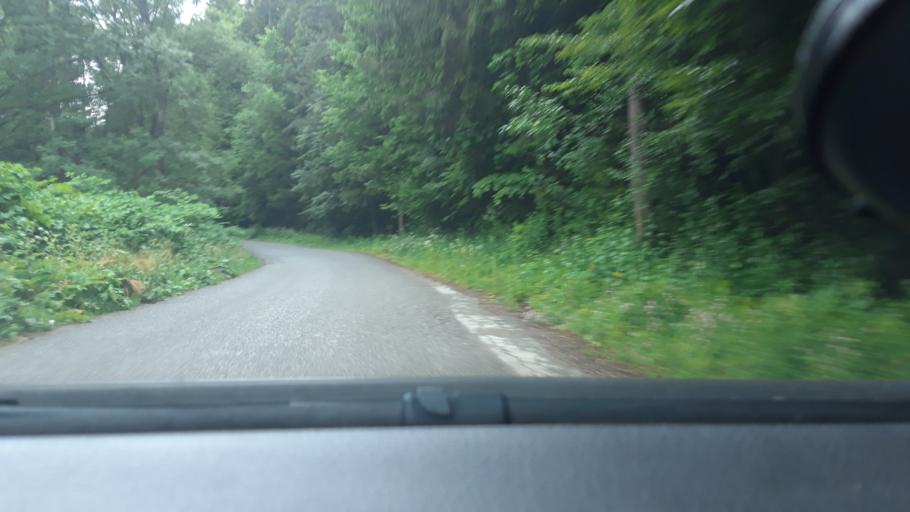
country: SK
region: Zilinsky
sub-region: Okres Martin
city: Martin
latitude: 49.0080
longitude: 18.9943
